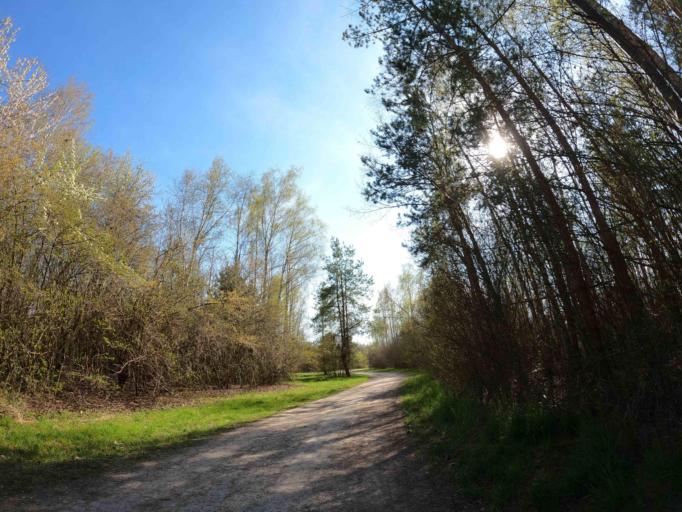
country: DE
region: Bavaria
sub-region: Upper Bavaria
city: Feldkirchen
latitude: 48.1351
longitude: 11.7173
